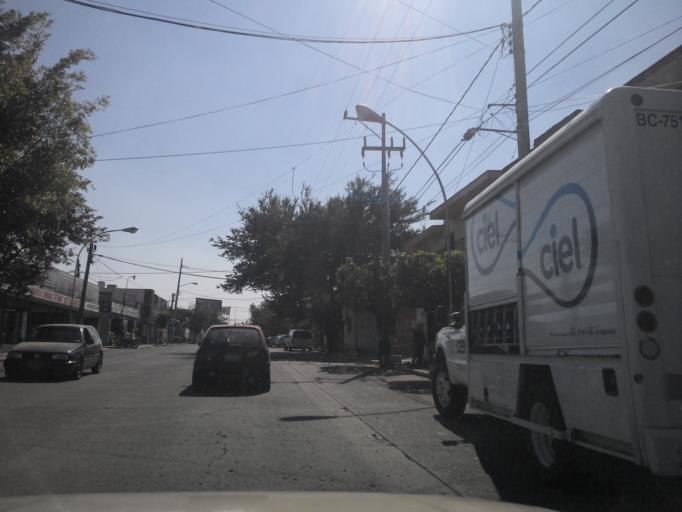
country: MX
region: Jalisco
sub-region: Zapopan
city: Zapopan
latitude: 20.6992
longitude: -103.3579
